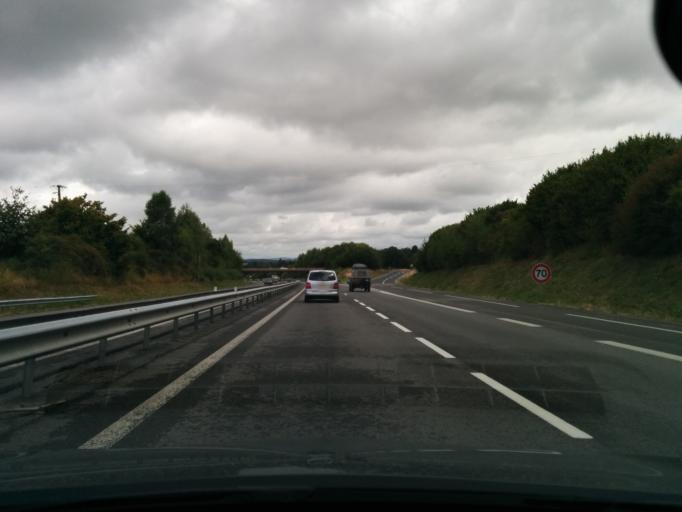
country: FR
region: Limousin
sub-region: Departement de la Correze
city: Uzerche
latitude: 45.4787
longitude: 1.5264
